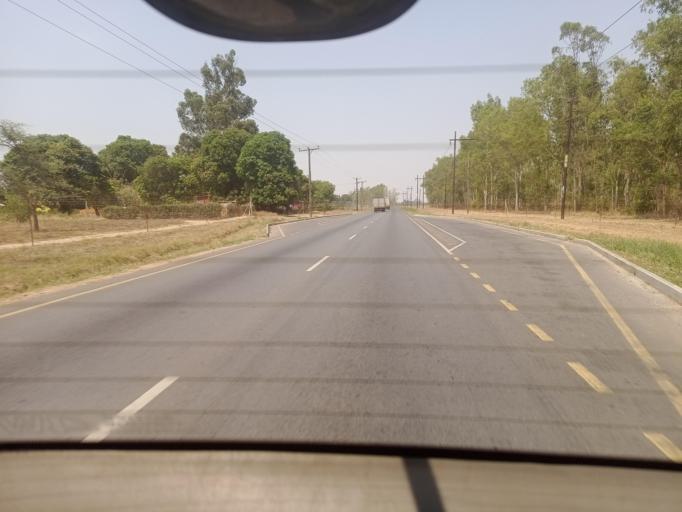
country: ZM
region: Lusaka
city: Lusaka
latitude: -15.2877
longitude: 28.3782
